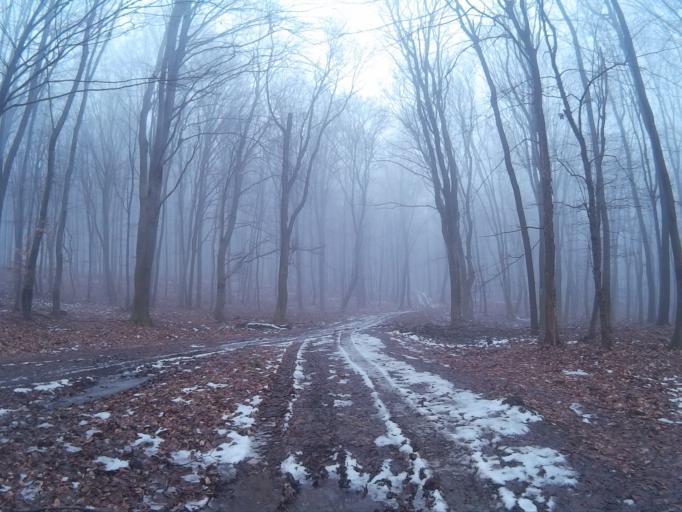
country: HU
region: Komarom-Esztergom
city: Tardos
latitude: 47.6802
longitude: 18.4717
